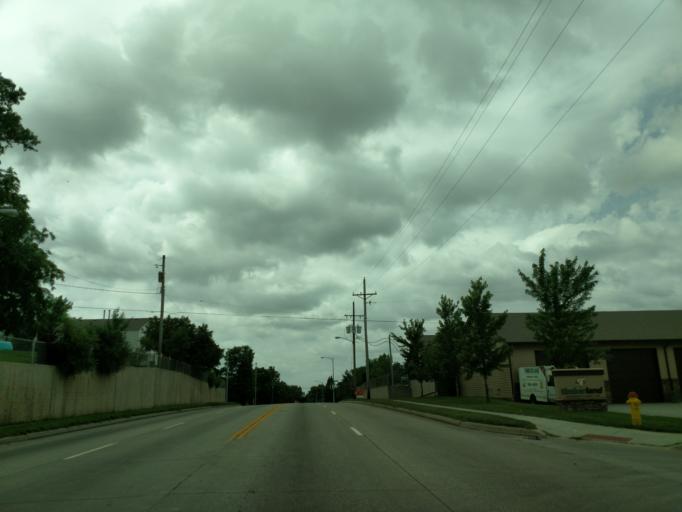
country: US
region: Nebraska
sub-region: Sarpy County
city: La Vista
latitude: 41.2101
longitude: -96.0047
